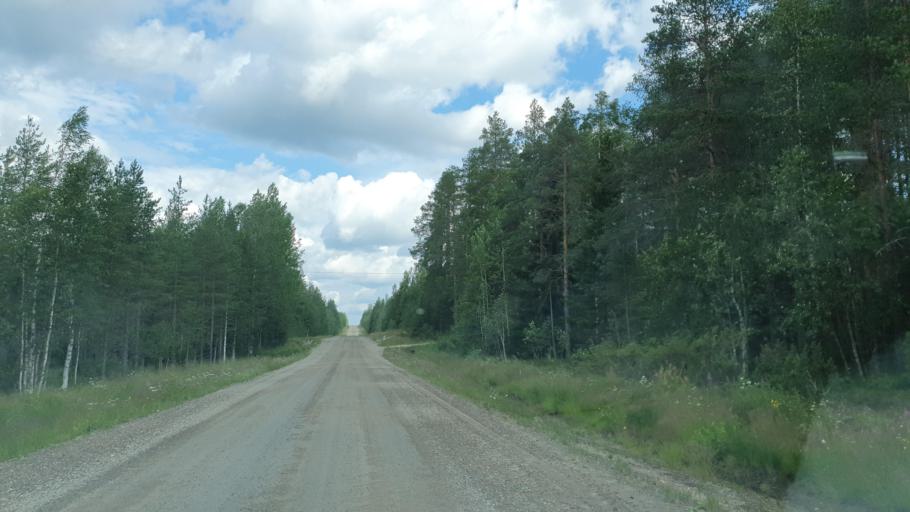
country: FI
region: Kainuu
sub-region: Kehys-Kainuu
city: Kuhmo
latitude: 64.4702
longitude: 29.5967
